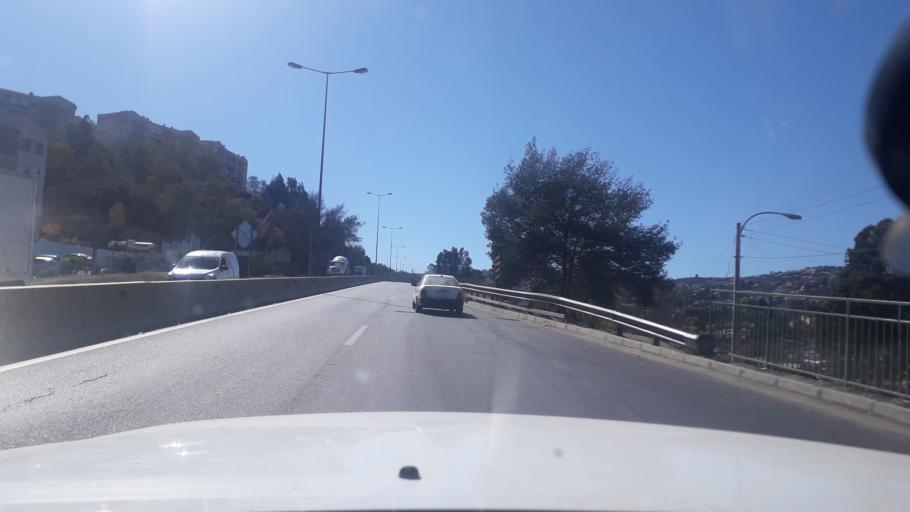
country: CL
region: Valparaiso
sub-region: Provincia de Valparaiso
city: Vina del Mar
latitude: -33.0348
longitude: -71.5014
